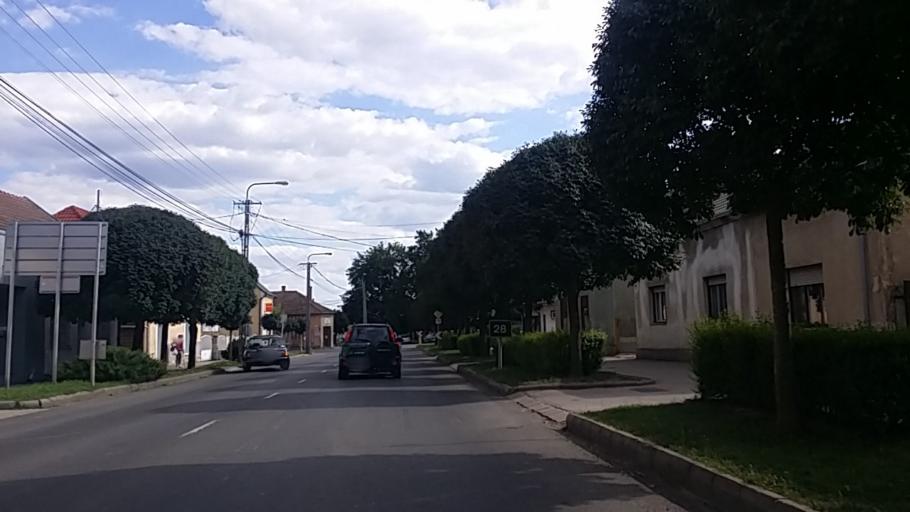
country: HU
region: Baranya
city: Sasd
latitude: 46.2538
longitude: 18.1061
